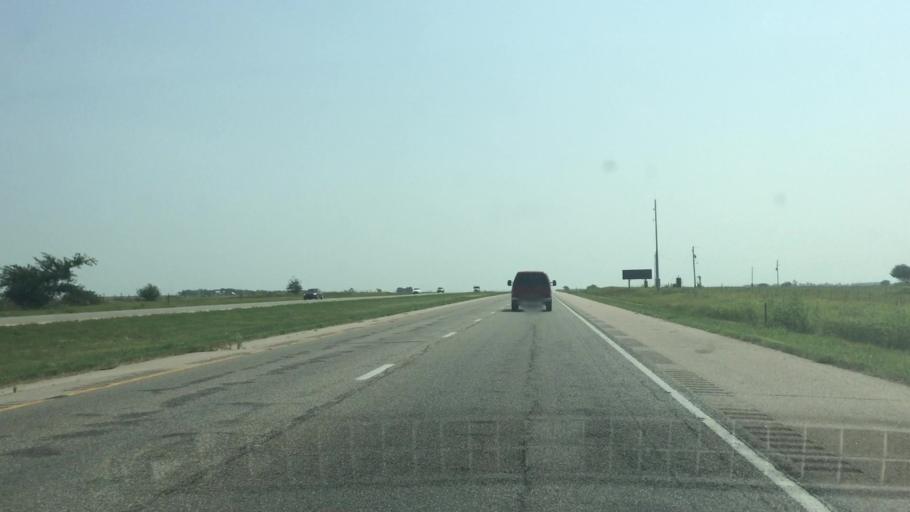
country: US
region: Kansas
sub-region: Osage County
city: Osage City
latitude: 38.4258
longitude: -95.8049
